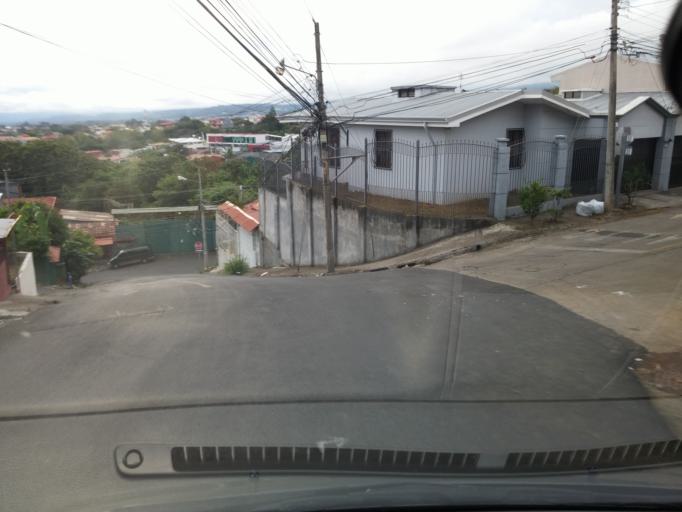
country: CR
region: Heredia
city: San Rafael
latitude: 10.0136
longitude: -84.1103
